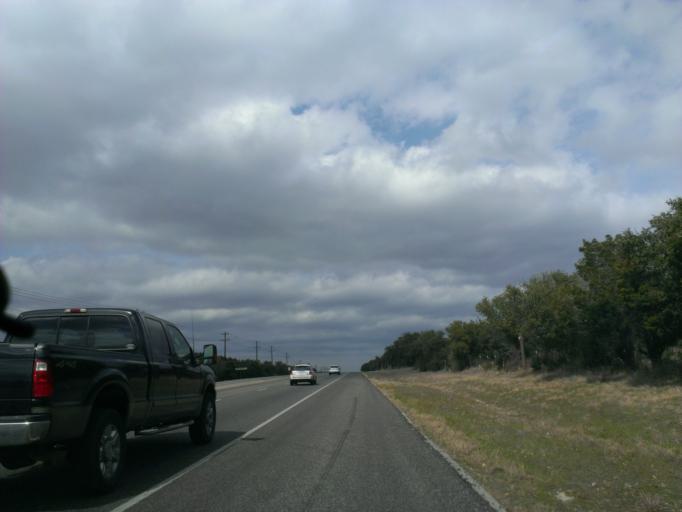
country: US
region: Texas
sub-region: Travis County
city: Briarcliff
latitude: 30.3789
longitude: -98.0818
